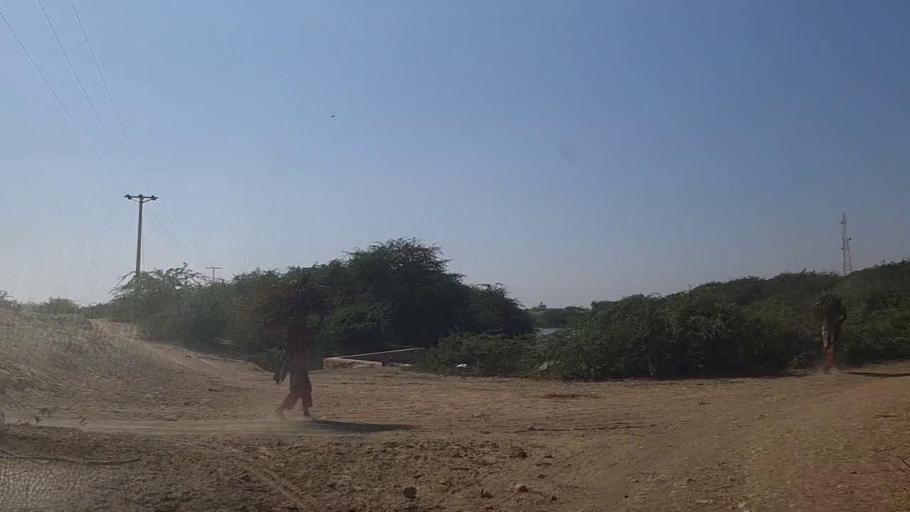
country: PK
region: Sindh
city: Daro Mehar
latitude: 24.8942
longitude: 68.0681
